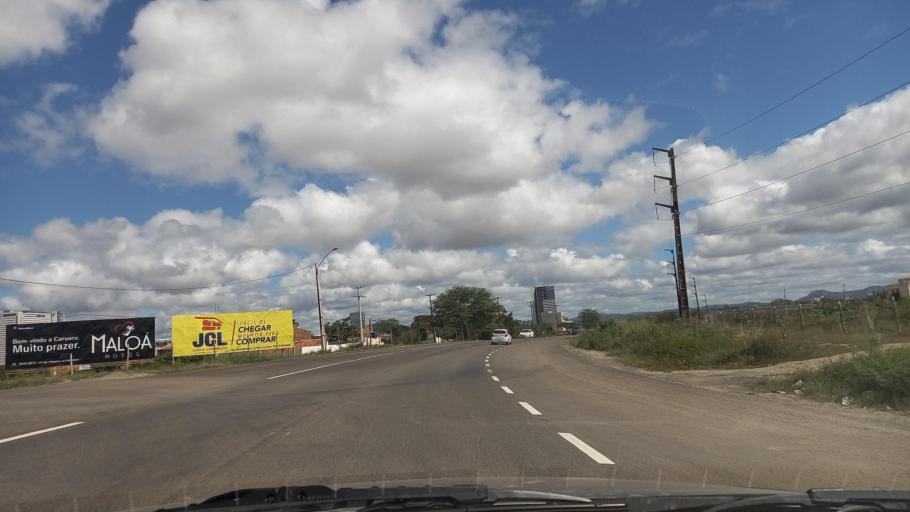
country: BR
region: Pernambuco
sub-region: Caruaru
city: Caruaru
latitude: -8.2577
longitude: -35.9544
